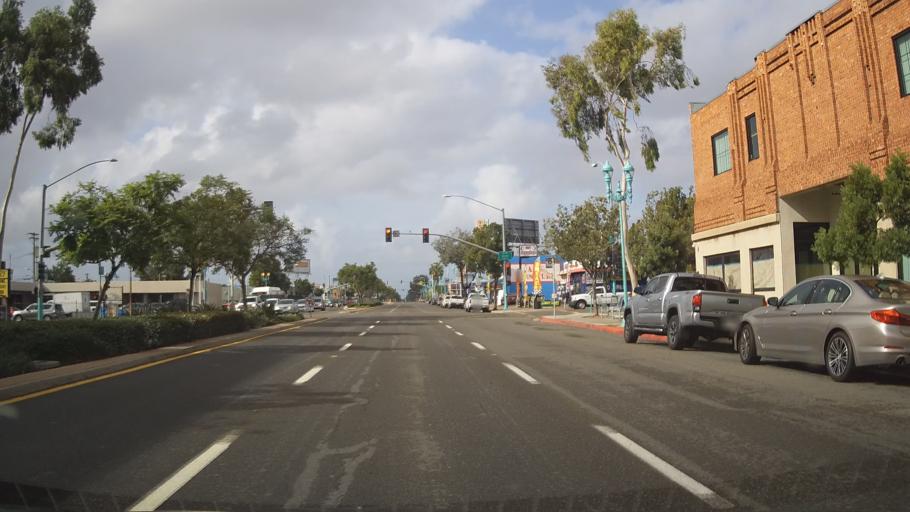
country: US
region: California
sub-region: San Diego County
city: San Diego
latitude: 32.7553
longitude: -117.1130
